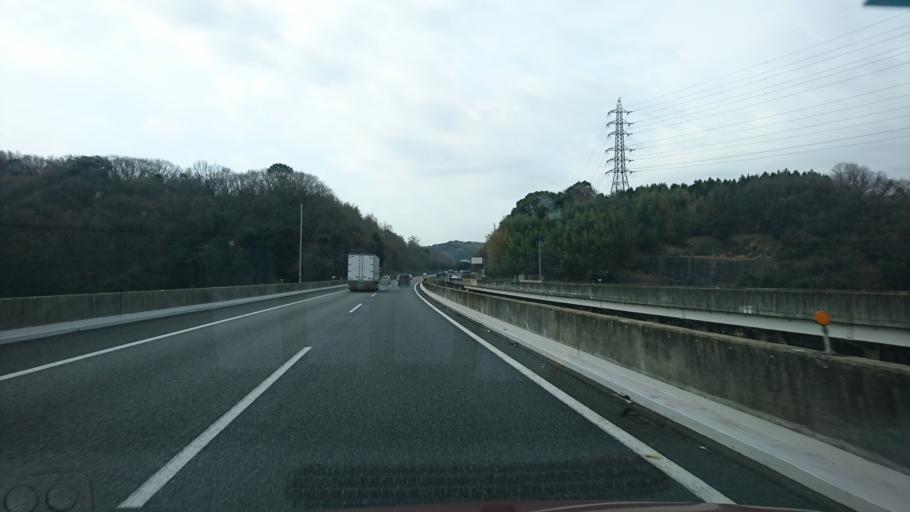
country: JP
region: Okayama
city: Kurashiki
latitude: 34.6068
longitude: 133.7287
